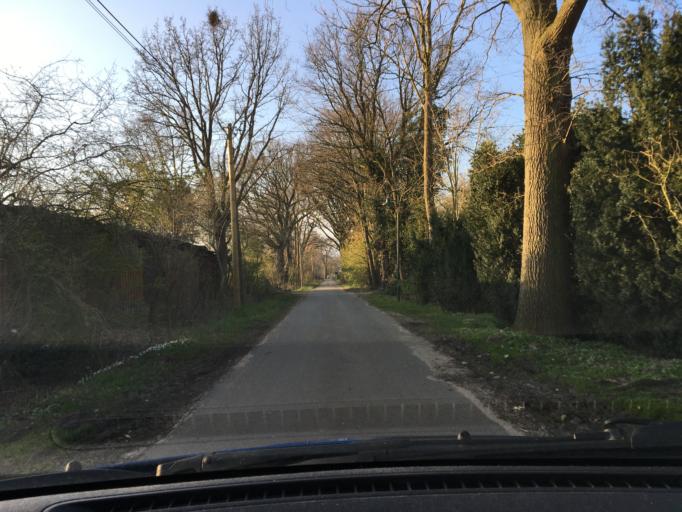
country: DE
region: Lower Saxony
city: Hittbergen
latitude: 53.3263
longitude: 10.6256
